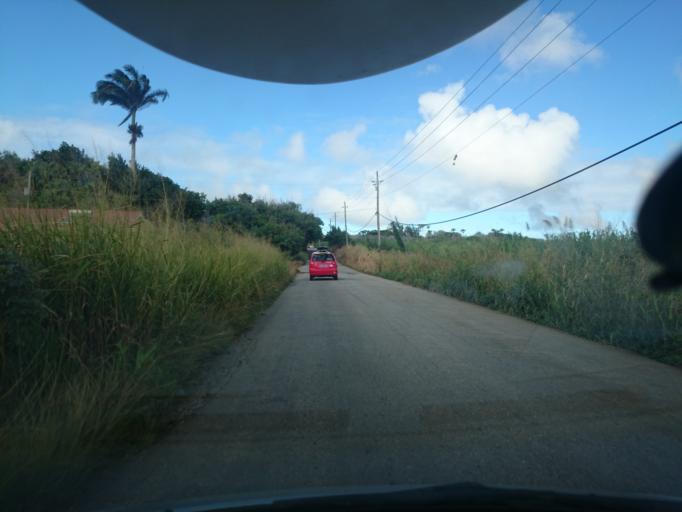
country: BB
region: Saint Thomas
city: Welchman Hall
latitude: 13.1806
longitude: -59.5453
